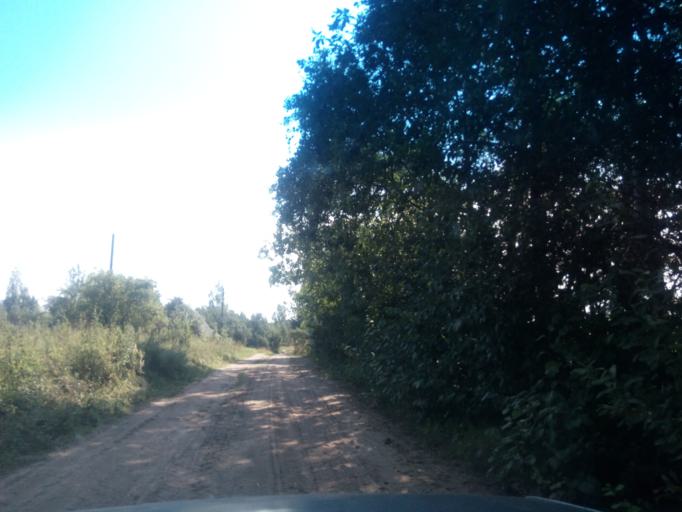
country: BY
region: Vitebsk
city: Dzisna
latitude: 55.6472
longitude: 28.2666
